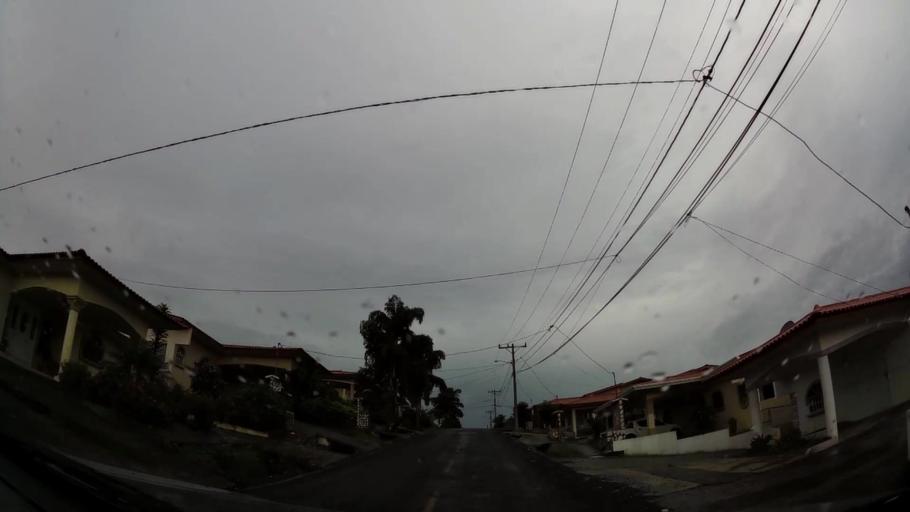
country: PA
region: Veraguas
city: Santiago de Veraguas
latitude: 8.0862
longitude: -80.9874
